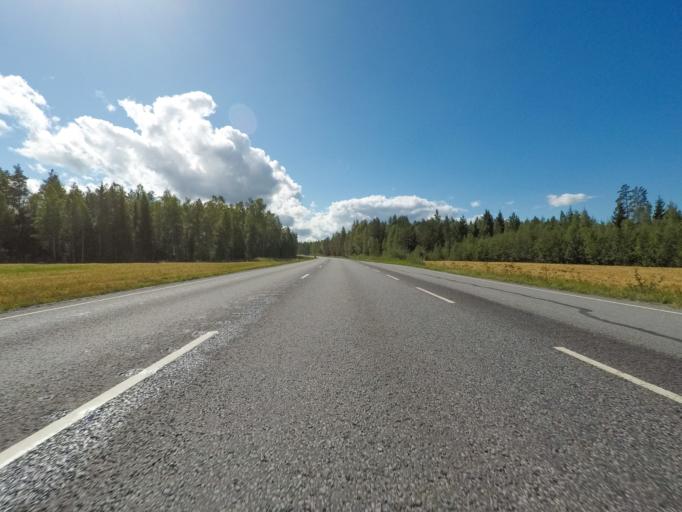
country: FI
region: Central Finland
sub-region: Jyvaeskylae
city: Hankasalmi
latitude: 62.3539
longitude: 26.5643
